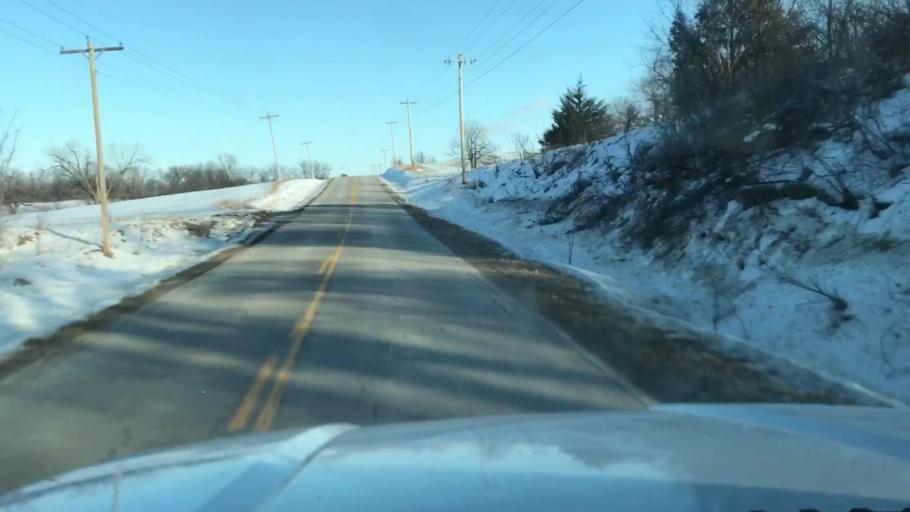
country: US
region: Missouri
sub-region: Andrew County
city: Savannah
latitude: 40.0246
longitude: -94.9031
